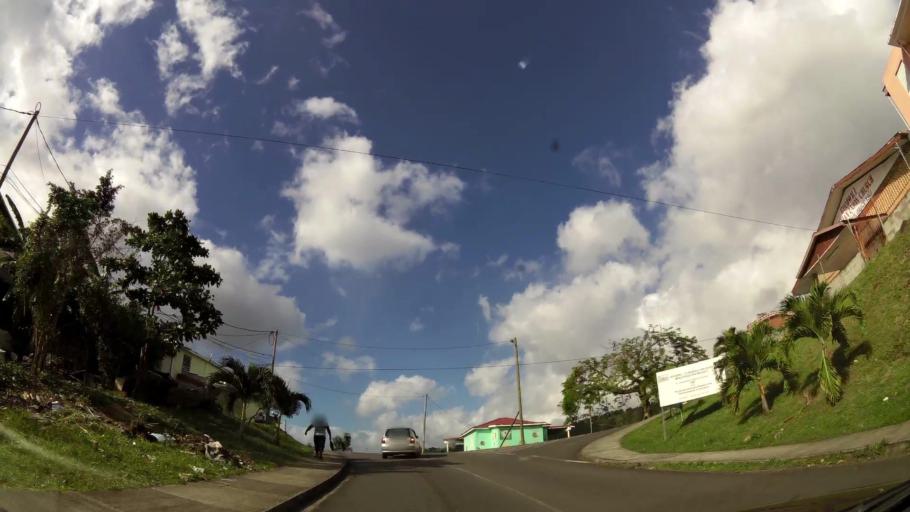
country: DM
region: Saint George
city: Roseau
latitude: 15.3038
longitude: -61.3855
